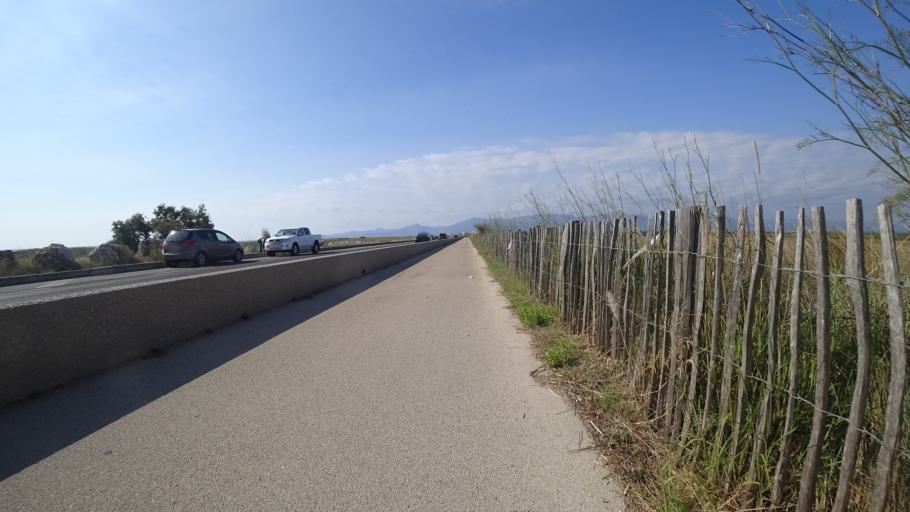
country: FR
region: Languedoc-Roussillon
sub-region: Departement des Pyrenees-Orientales
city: Saint-Cyprien-Plage
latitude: 42.6554
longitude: 3.0328
